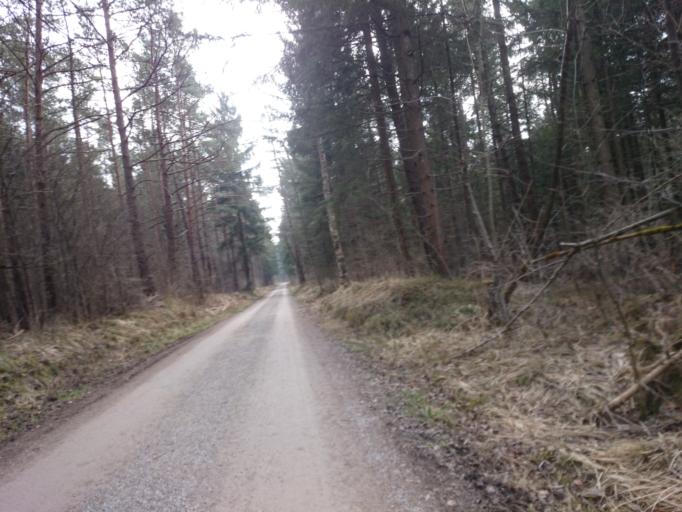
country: DE
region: Bavaria
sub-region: Swabia
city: Konigsbrunn
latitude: 48.2834
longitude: 10.9141
